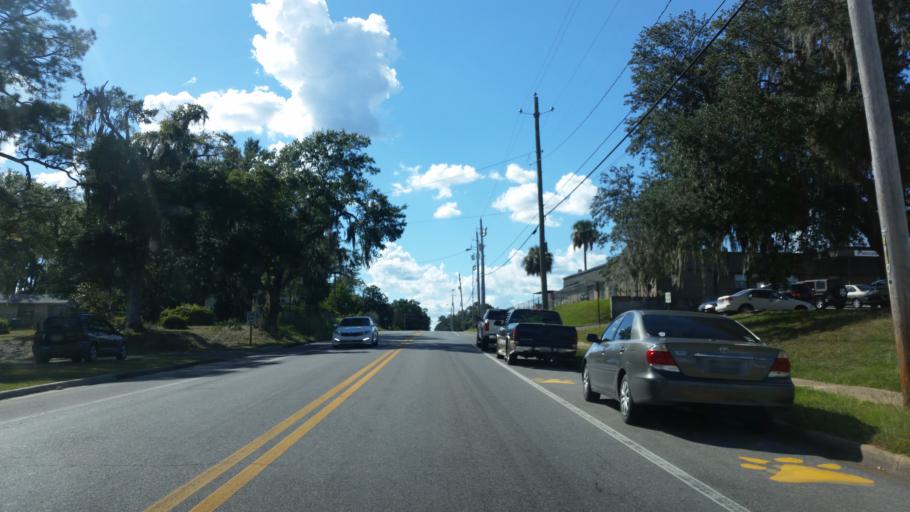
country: US
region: Florida
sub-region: Santa Rosa County
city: Milton
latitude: 30.6308
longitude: -87.0444
